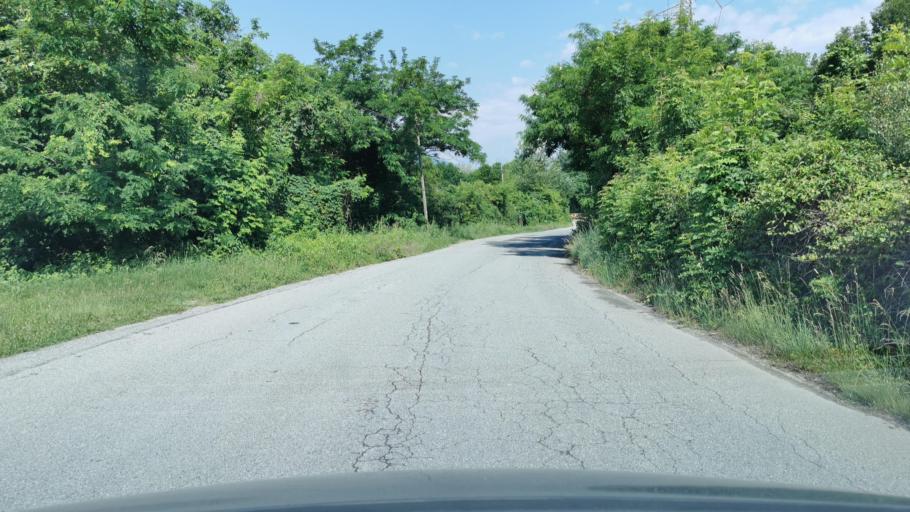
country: IT
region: Piedmont
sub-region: Provincia di Torino
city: Villanova Canavese
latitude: 45.2415
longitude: 7.5490
